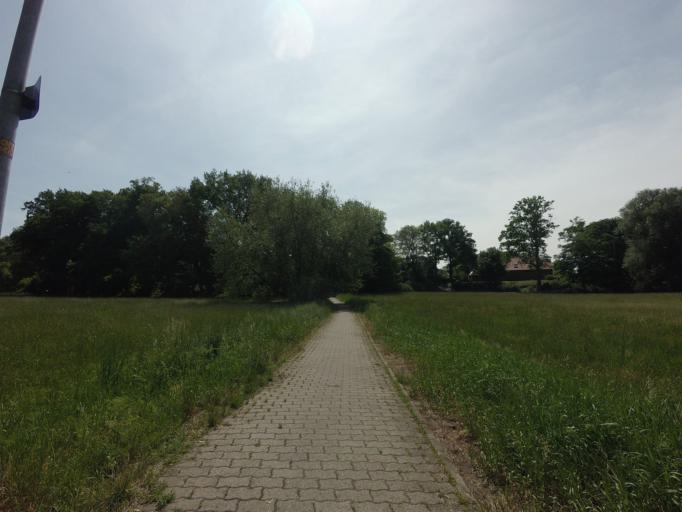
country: DE
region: Lower Saxony
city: Klein Schwulper
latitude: 52.3436
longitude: 10.4454
